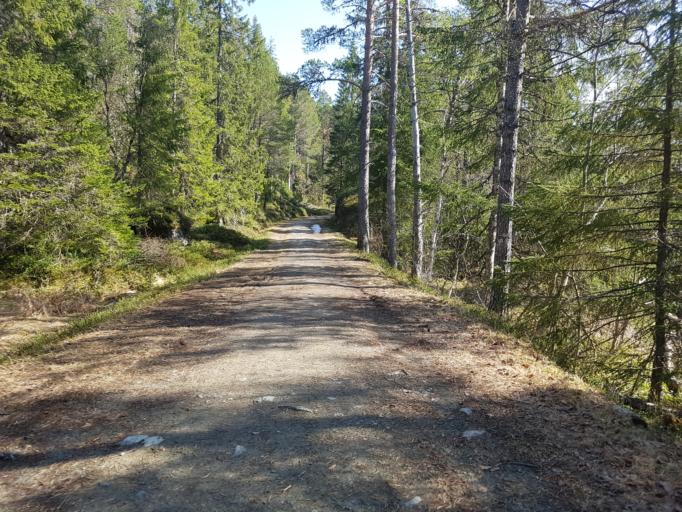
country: NO
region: Sor-Trondelag
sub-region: Trondheim
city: Trondheim
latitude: 63.4338
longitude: 10.2920
